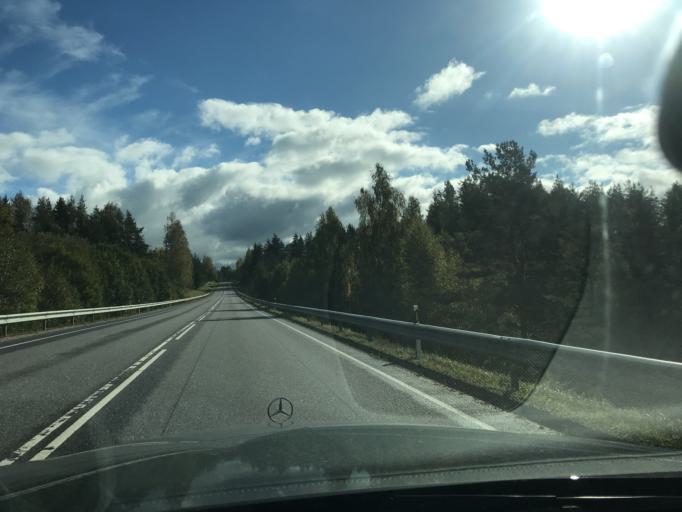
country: EE
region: Vorumaa
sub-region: Voru linn
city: Voru
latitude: 57.8034
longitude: 27.0835
